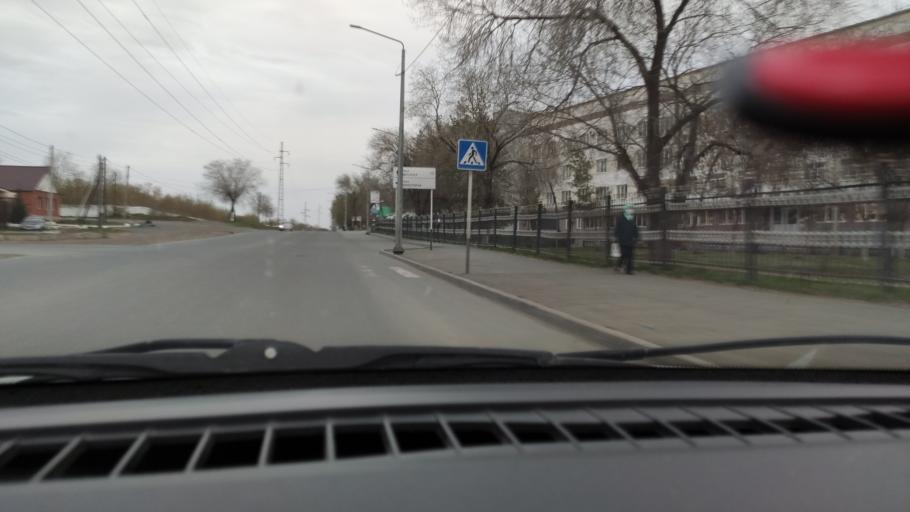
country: RU
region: Orenburg
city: Orenburg
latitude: 51.7853
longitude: 55.1142
